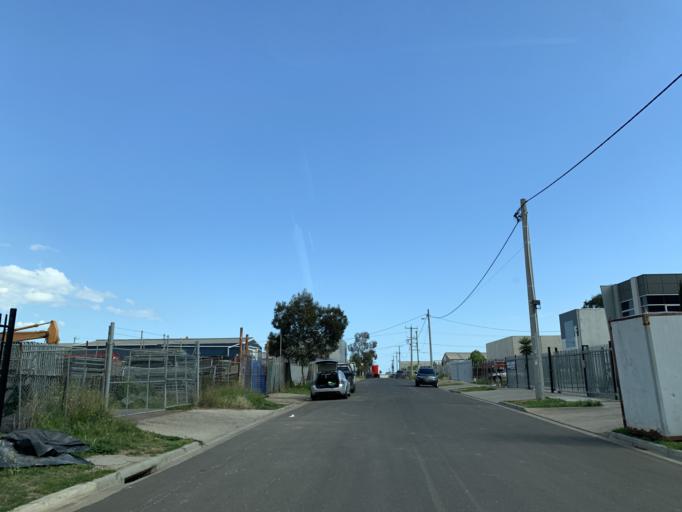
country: AU
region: Victoria
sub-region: Brimbank
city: Kealba
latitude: -37.7502
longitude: 144.8389
